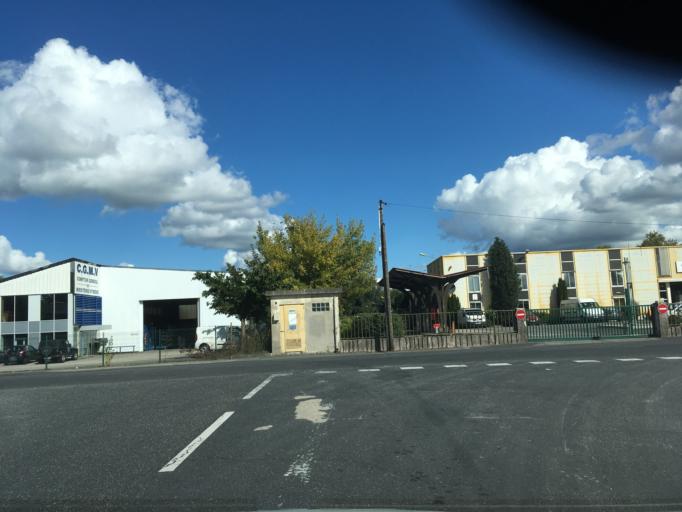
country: FR
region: Limousin
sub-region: Departement de la Correze
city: Saint-Pantaleon-de-Larche
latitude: 45.1524
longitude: 1.4805
